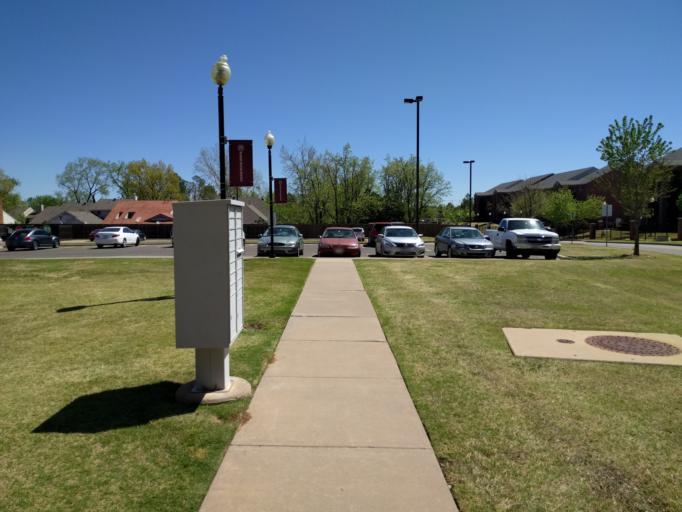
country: US
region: Oklahoma
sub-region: Oklahoma County
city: Edmond
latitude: 35.6110
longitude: -97.4633
